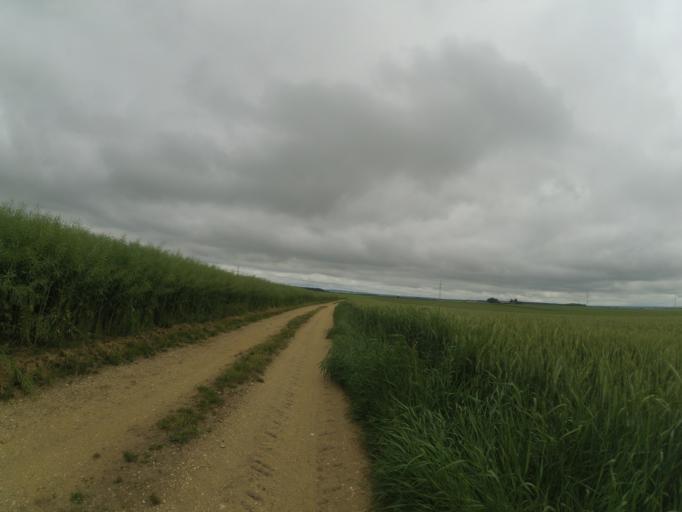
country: DE
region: Baden-Wuerttemberg
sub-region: Tuebingen Region
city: Bernstadt
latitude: 48.4636
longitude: 10.0449
